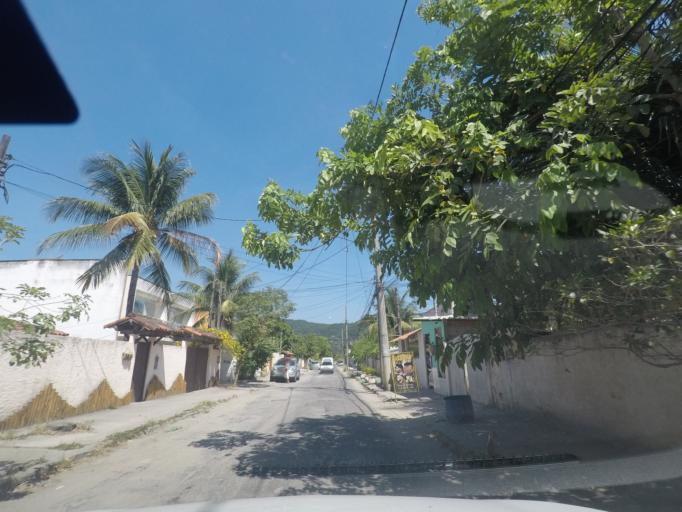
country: BR
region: Rio de Janeiro
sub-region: Niteroi
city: Niteroi
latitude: -22.9383
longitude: -43.0280
